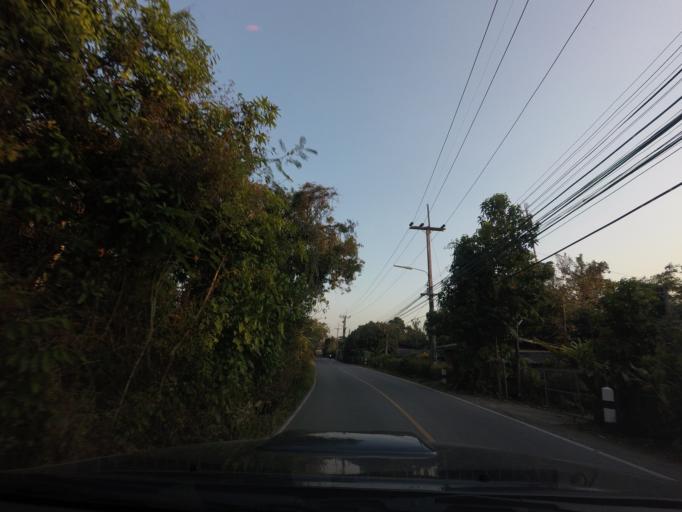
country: TH
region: Chiang Mai
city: Chiang Mai
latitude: 18.9197
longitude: 98.9119
